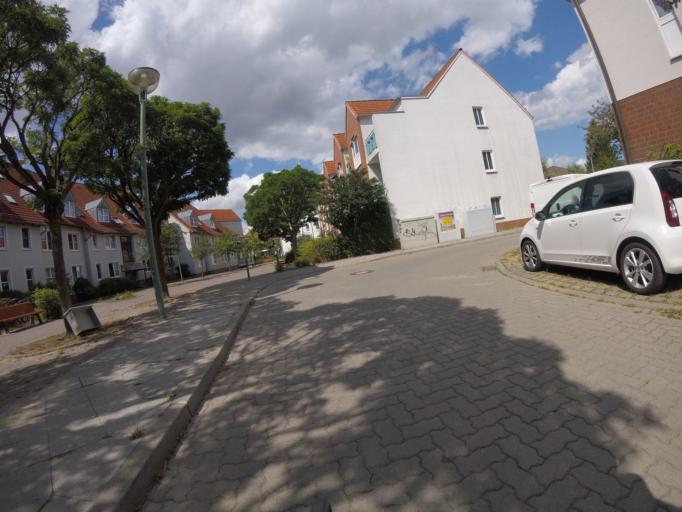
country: DE
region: Brandenburg
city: Werder
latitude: 52.4103
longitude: 12.9921
